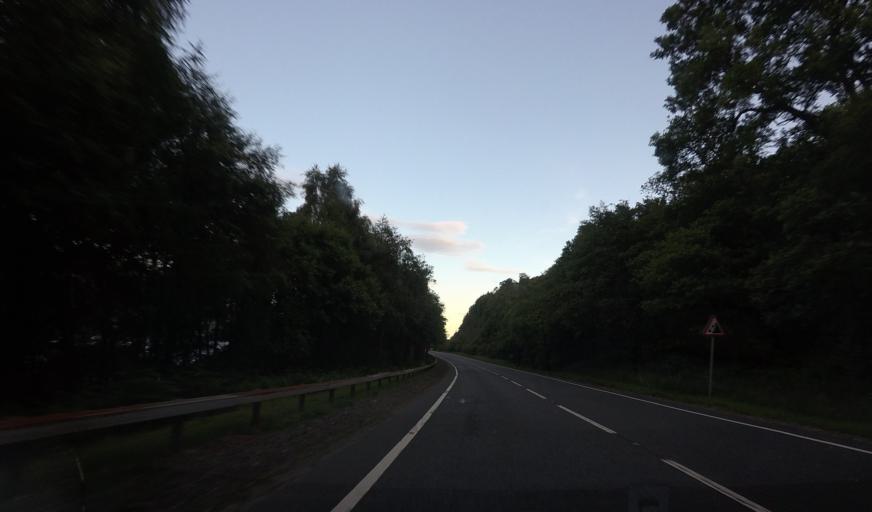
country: GB
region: Scotland
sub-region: Argyll and Bute
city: Garelochhead
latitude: 56.1803
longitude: -4.6894
